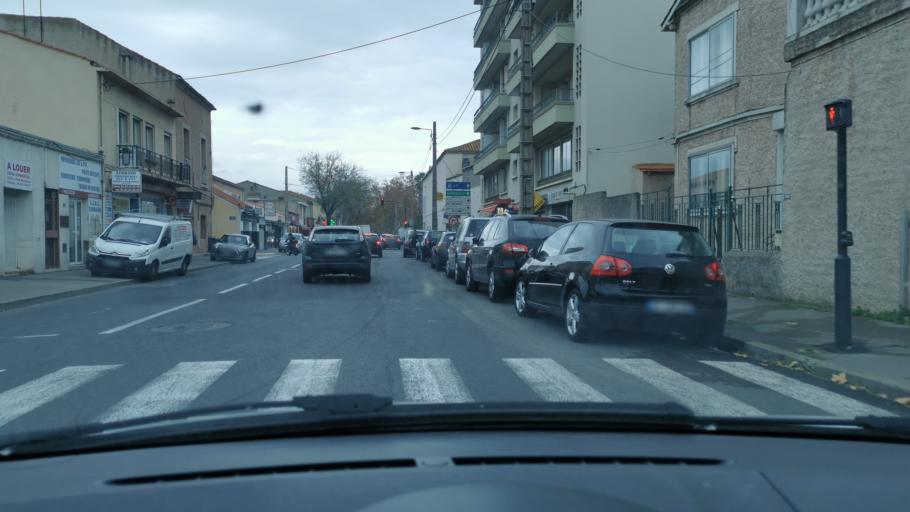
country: FR
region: Languedoc-Roussillon
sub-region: Departement de l'Herault
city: Sete
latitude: 43.4105
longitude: 3.6777
